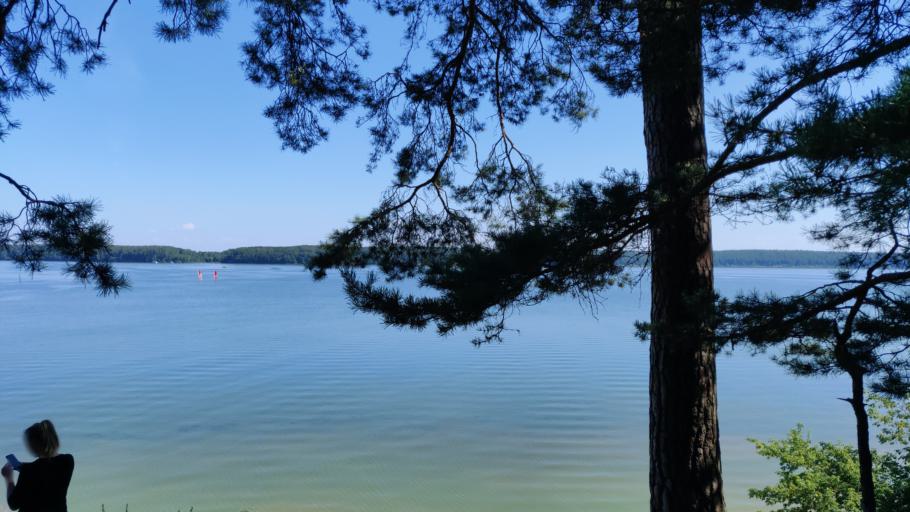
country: LT
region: Kauno apskritis
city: Dainava (Kaunas)
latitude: 54.8827
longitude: 24.0238
